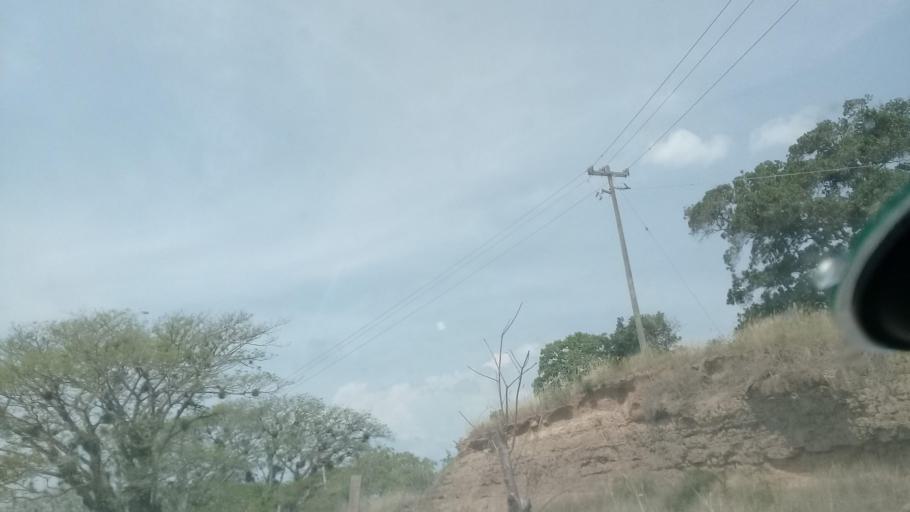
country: MX
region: Veracruz
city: El Castillo
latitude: 19.5265
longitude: -96.8581
